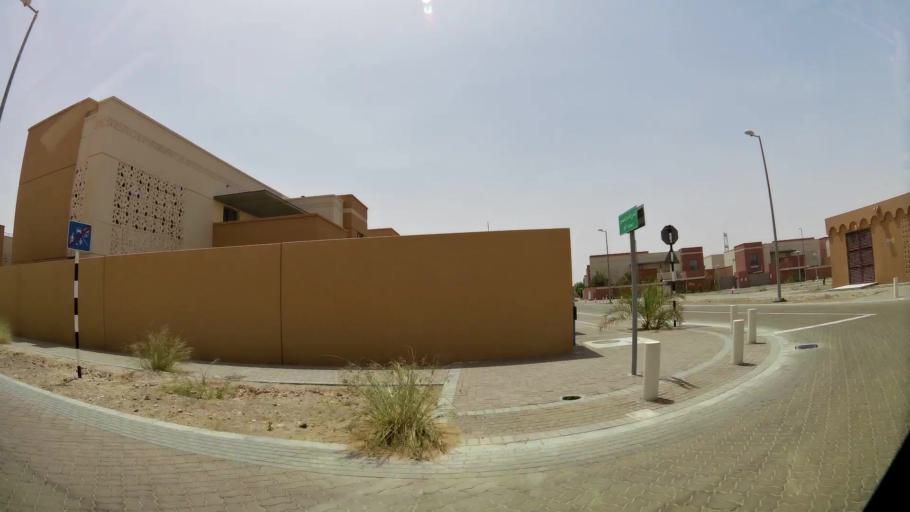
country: AE
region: Abu Dhabi
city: Al Ain
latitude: 24.1423
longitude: 55.6193
